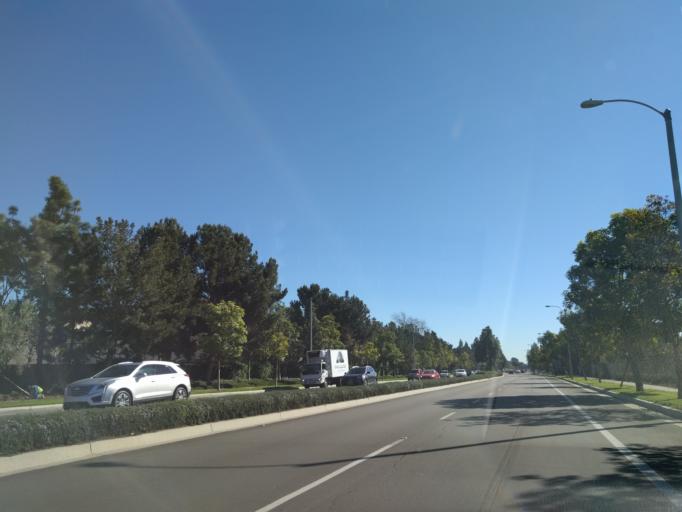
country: US
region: California
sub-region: Orange County
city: North Tustin
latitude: 33.7180
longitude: -117.7797
